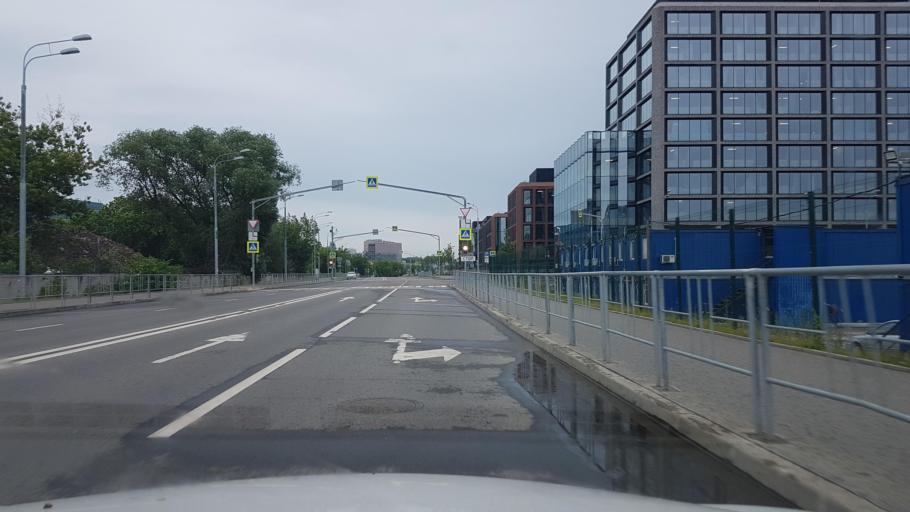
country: RU
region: Moscow
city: Strogino
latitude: 55.8235
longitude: 37.4228
